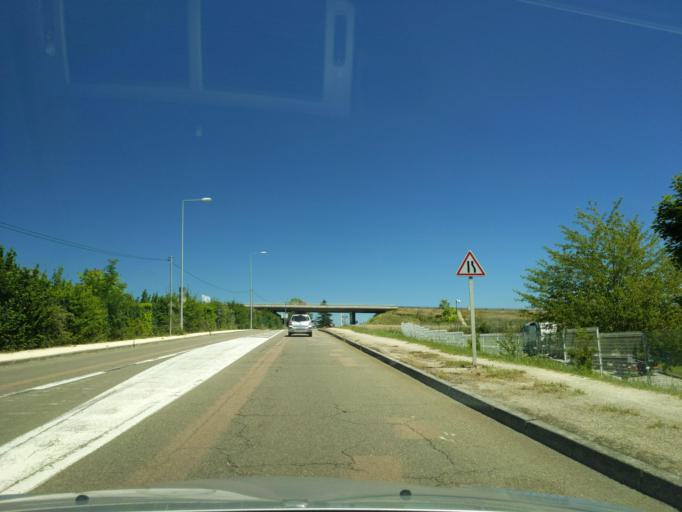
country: FR
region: Bourgogne
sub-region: Departement de la Cote-d'Or
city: Ruffey-les-Echirey
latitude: 47.3561
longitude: 5.0641
